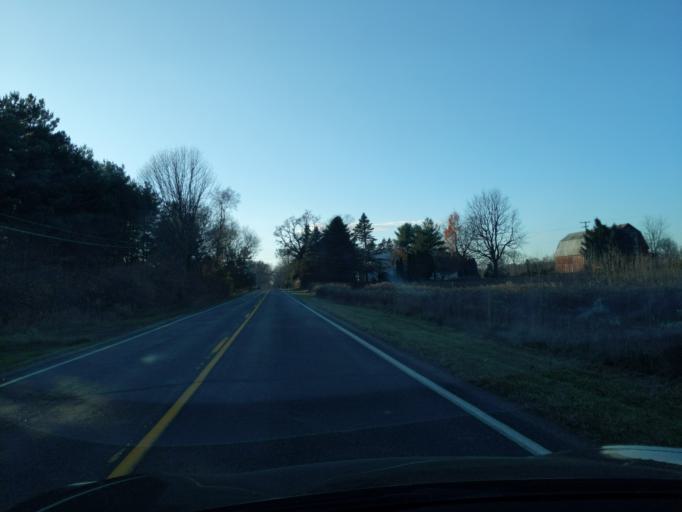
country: US
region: Michigan
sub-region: Ingham County
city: Williamston
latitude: 42.7155
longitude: -84.3208
